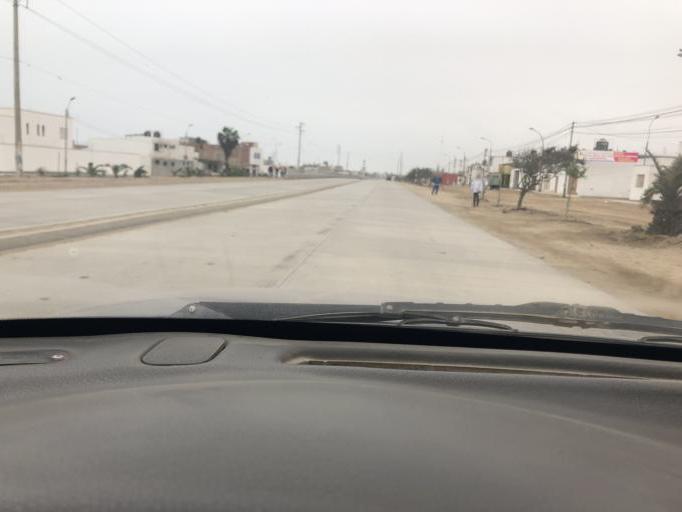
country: PE
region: Lima
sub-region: Lima
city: San Bartolo
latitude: -12.3710
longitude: -76.7887
